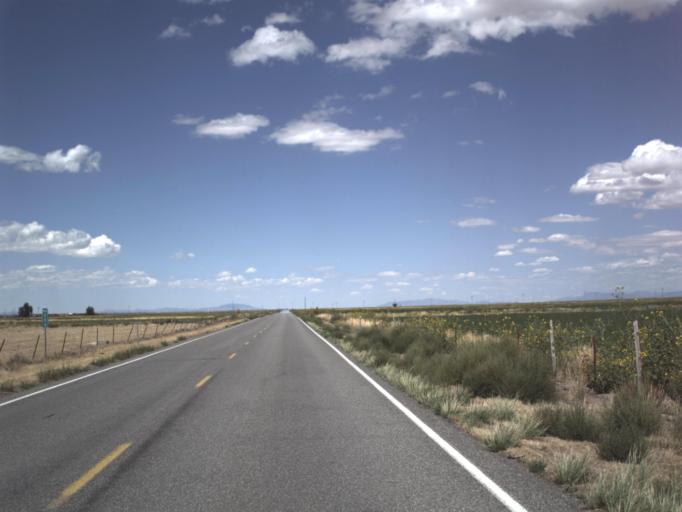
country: US
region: Utah
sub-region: Millard County
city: Delta
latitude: 39.2060
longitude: -112.4114
